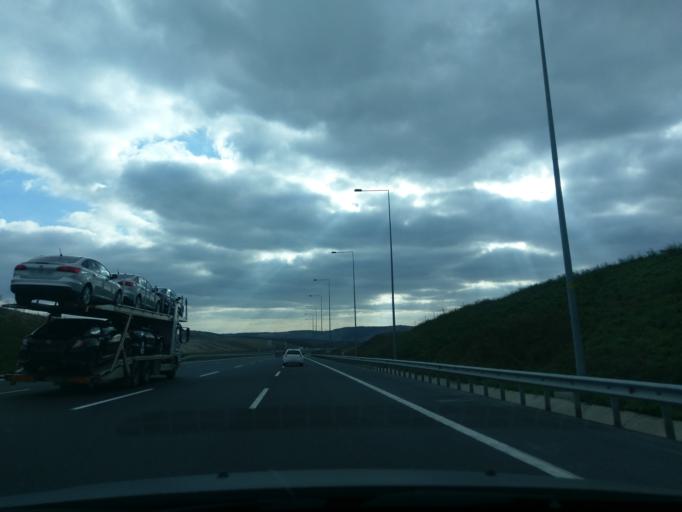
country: TR
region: Istanbul
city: Kemerburgaz
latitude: 41.2303
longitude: 28.8416
